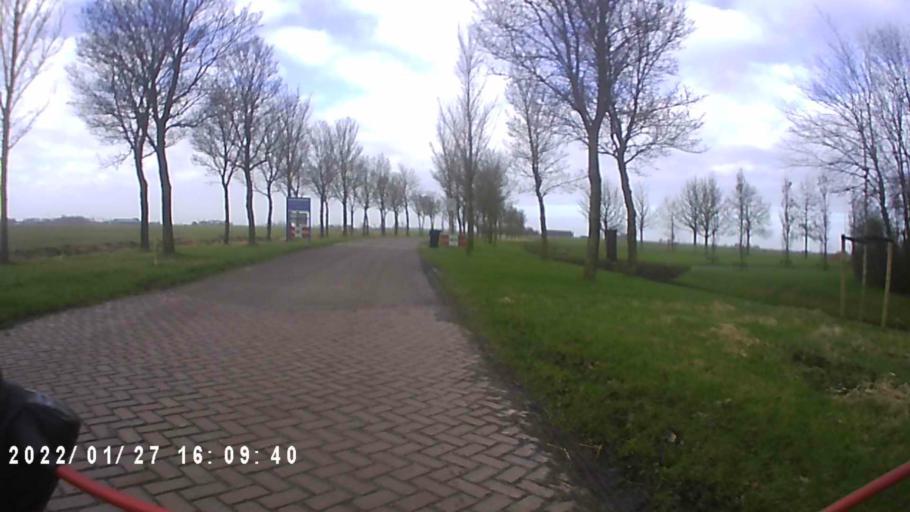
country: NL
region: Friesland
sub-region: Gemeente Dongeradeel
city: Anjum
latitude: 53.3806
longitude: 6.0826
